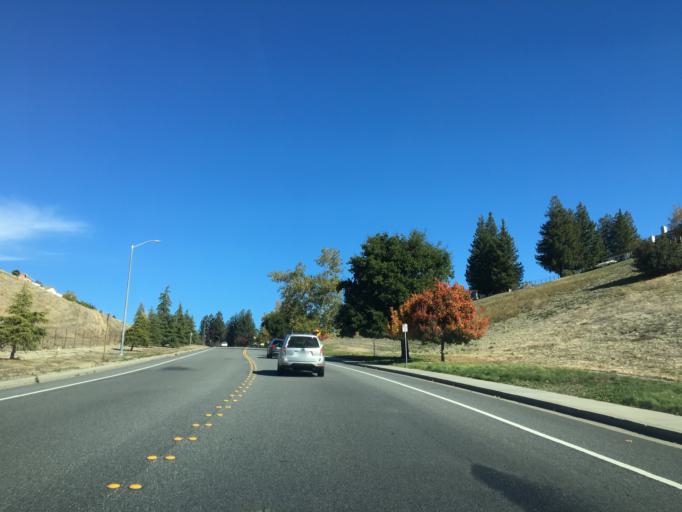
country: US
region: California
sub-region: Alameda County
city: Fremont
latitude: 37.5167
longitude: -121.9264
